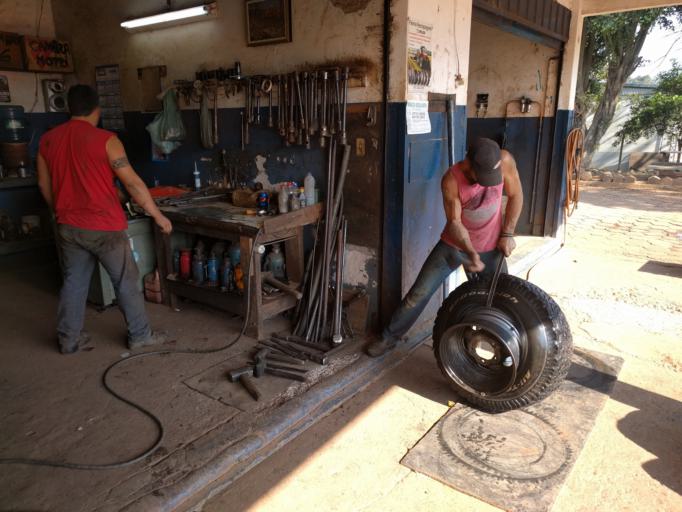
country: BR
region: Sao Paulo
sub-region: Paranapanema
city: Paranapanema
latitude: -23.4318
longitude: -48.8714
